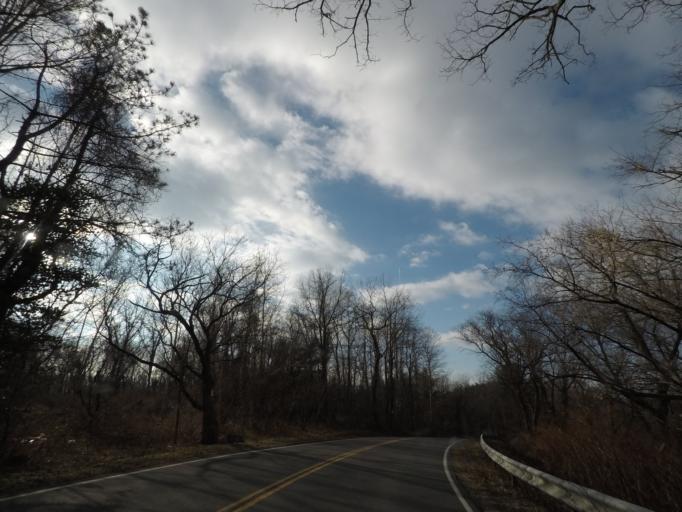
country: US
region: New York
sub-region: Albany County
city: Westmere
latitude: 42.6620
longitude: -73.8765
